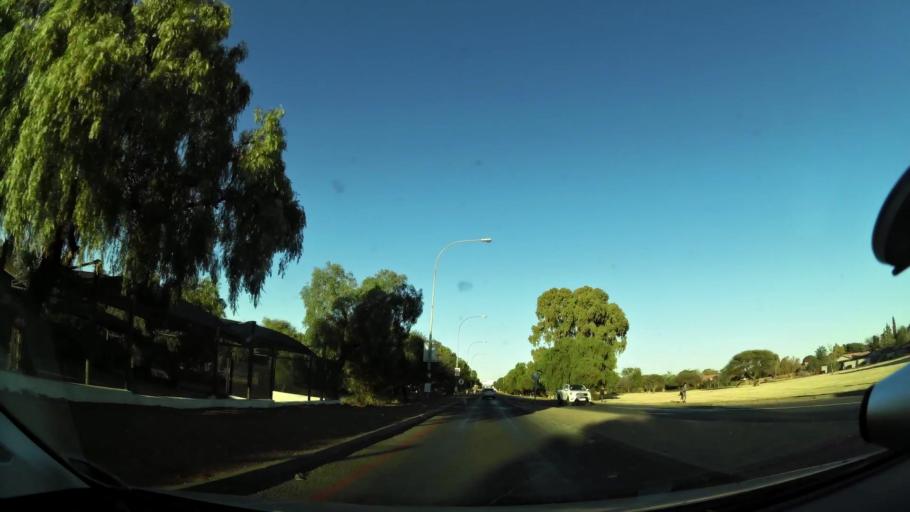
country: ZA
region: Northern Cape
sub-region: Frances Baard District Municipality
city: Kimberley
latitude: -28.7618
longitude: 24.7589
